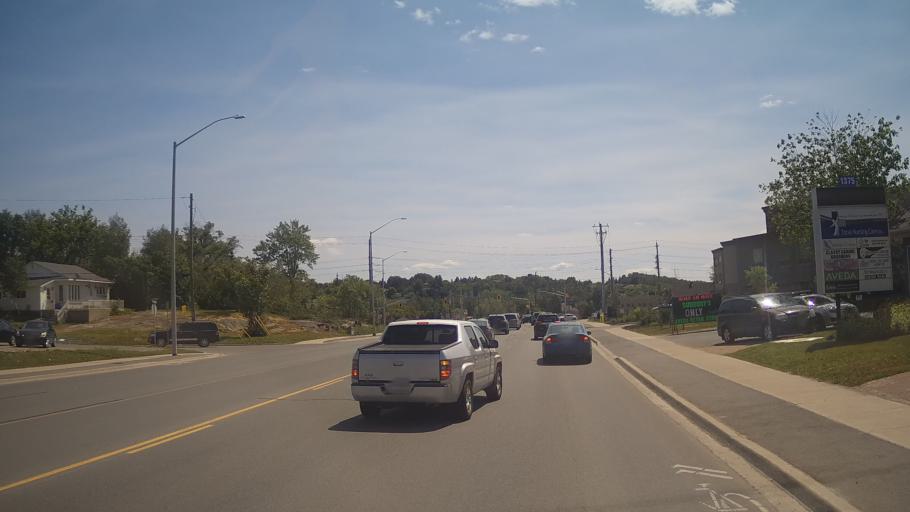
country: CA
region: Ontario
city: Greater Sudbury
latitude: 46.4623
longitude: -81.0097
